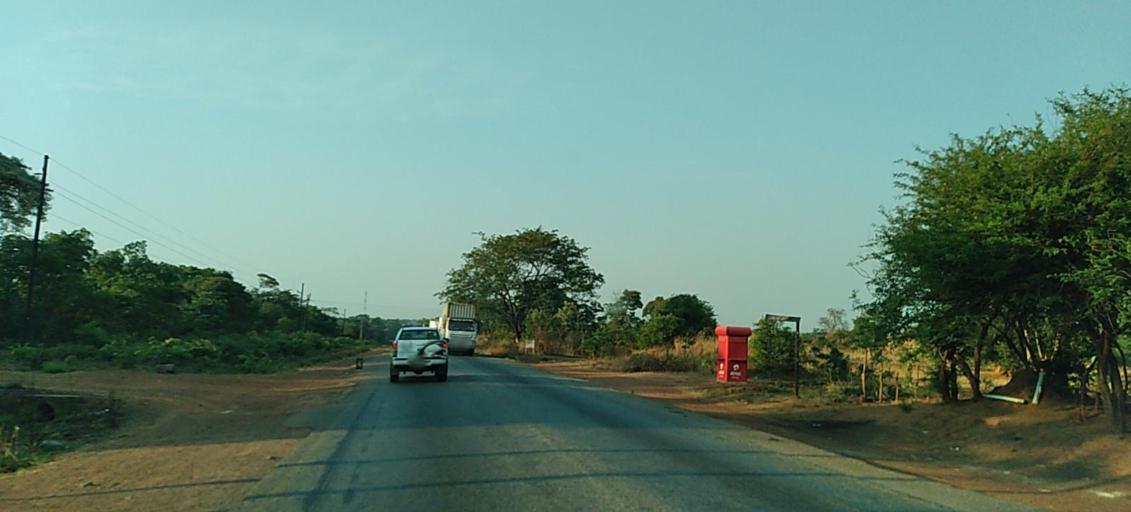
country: ZM
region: Copperbelt
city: Ndola
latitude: -13.1666
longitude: 28.6968
